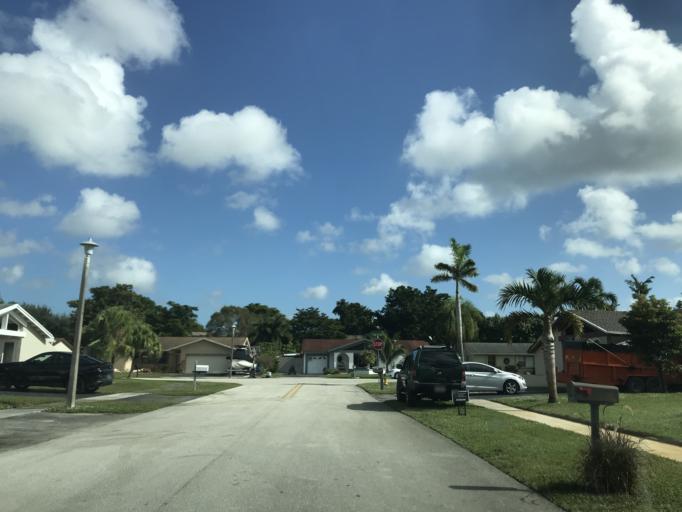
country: US
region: Florida
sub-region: Broward County
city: Coconut Creek
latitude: 26.2679
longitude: -80.1935
